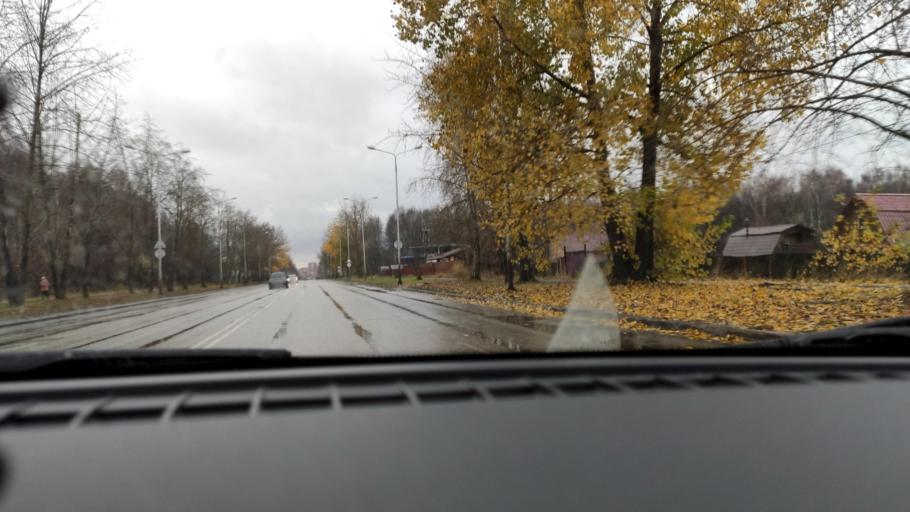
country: RU
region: Perm
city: Perm
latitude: 58.0827
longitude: 56.3755
